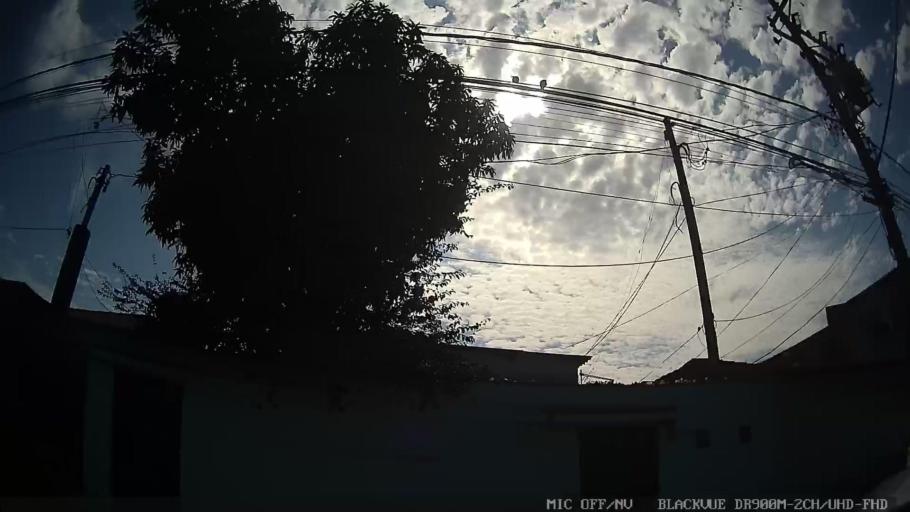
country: BR
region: Sao Paulo
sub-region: Santos
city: Santos
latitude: -23.9451
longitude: -46.2895
